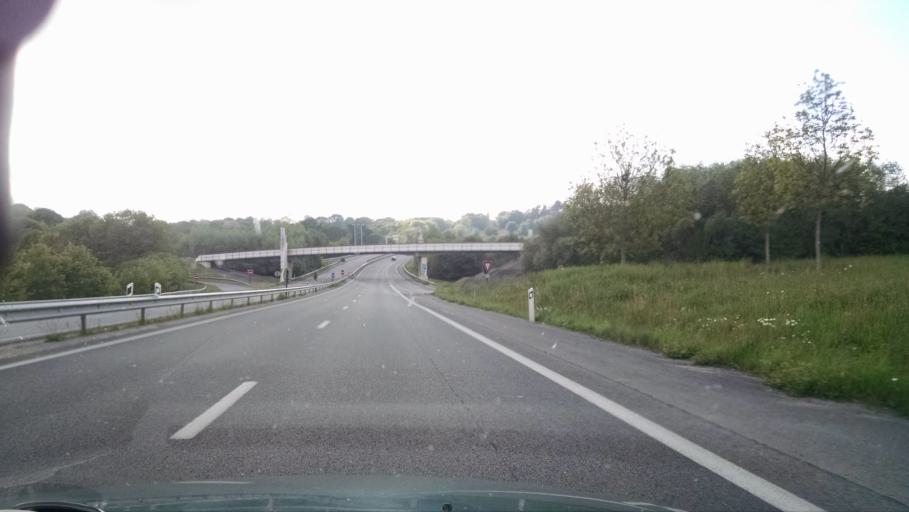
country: FR
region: Brittany
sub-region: Departement du Finistere
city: Taule
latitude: 48.5823
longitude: -3.8703
